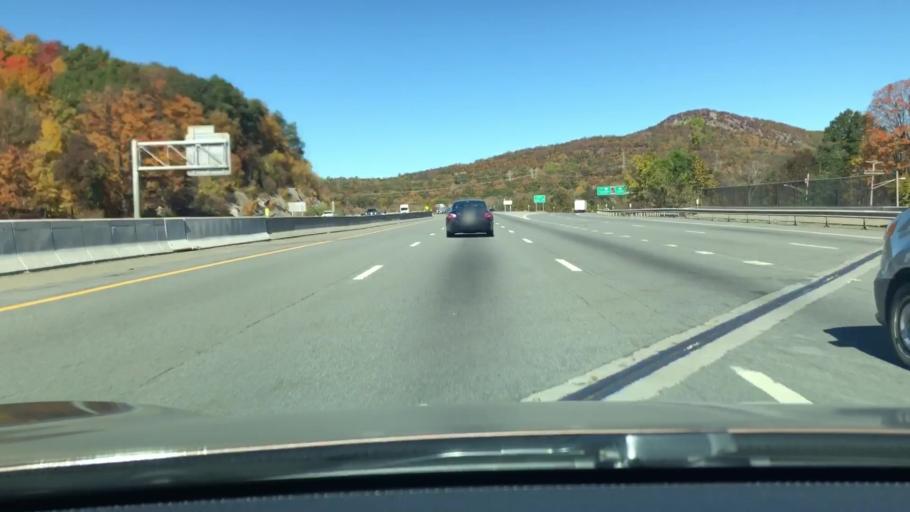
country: US
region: New York
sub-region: Rockland County
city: Suffern
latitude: 41.1340
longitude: -74.1681
